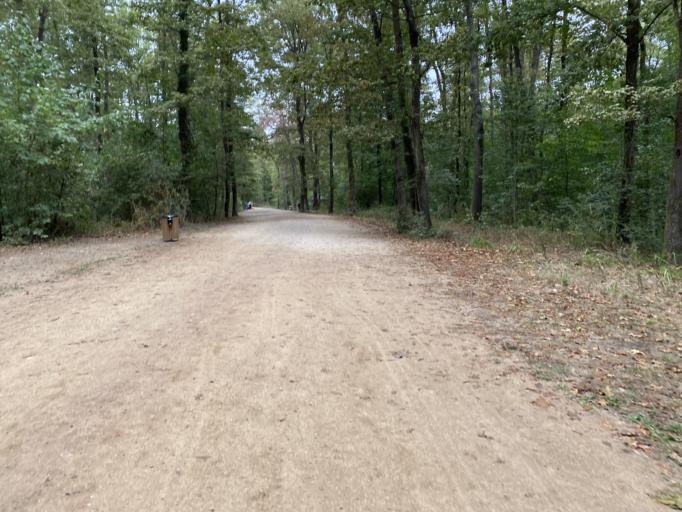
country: TR
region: Kocaeli
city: Derbent
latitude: 40.7356
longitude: 30.1671
